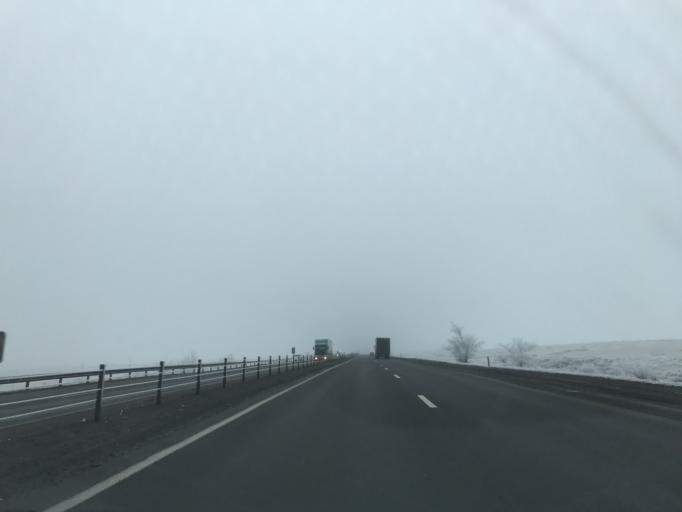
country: RU
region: Rostov
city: Likhoy
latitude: 48.1506
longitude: 40.2609
